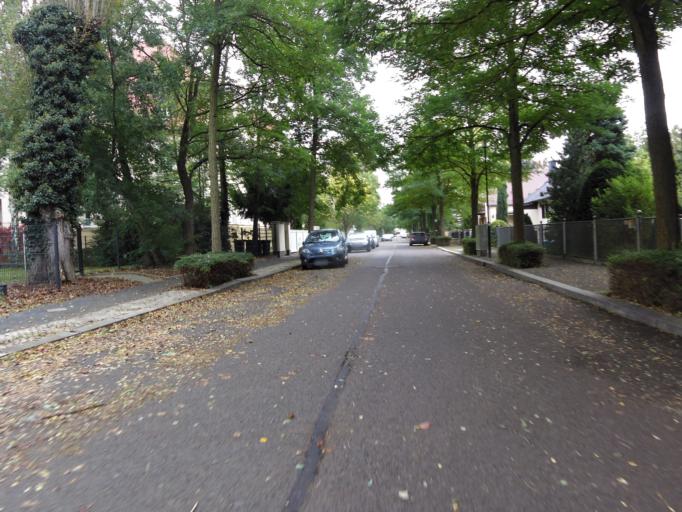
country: DE
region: Saxony
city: Markkleeberg
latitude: 51.2832
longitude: 12.3683
